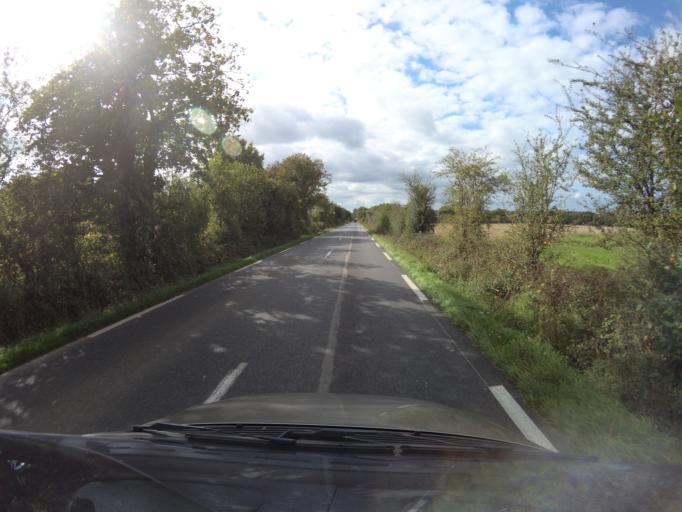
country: FR
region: Pays de la Loire
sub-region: Departement de la Loire-Atlantique
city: Notre-Dame-des-Landes
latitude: 47.4083
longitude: -1.7248
